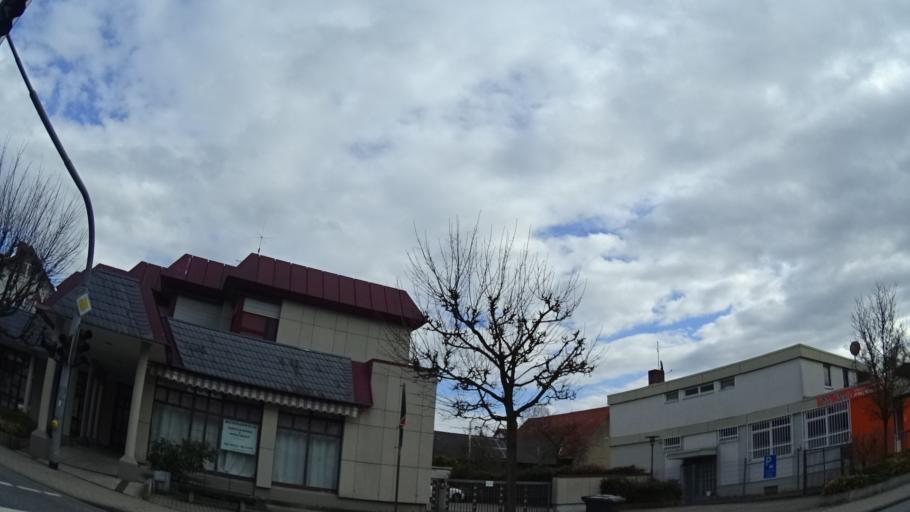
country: DE
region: Hesse
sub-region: Regierungsbezirk Darmstadt
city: Gross-Gerau
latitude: 49.8769
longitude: 8.4819
